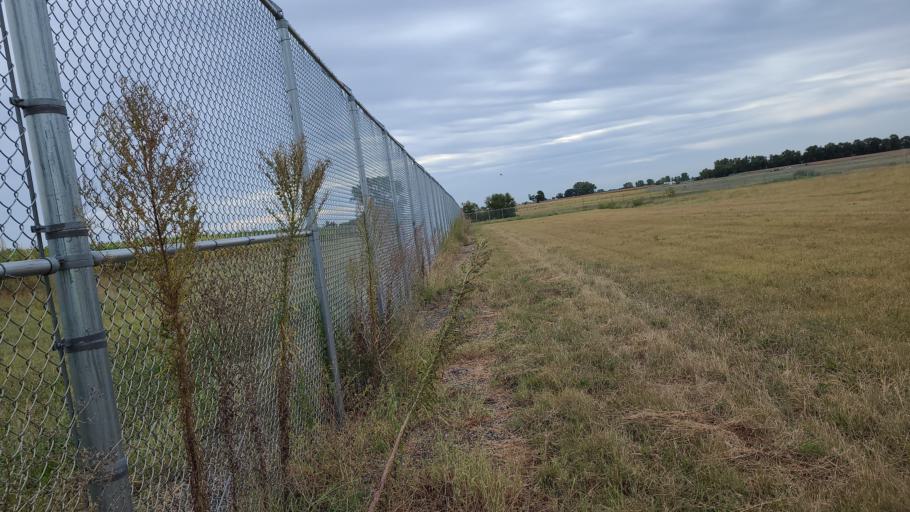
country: US
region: Kansas
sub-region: Douglas County
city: Lawrence
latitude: 39.0060
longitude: -95.2089
